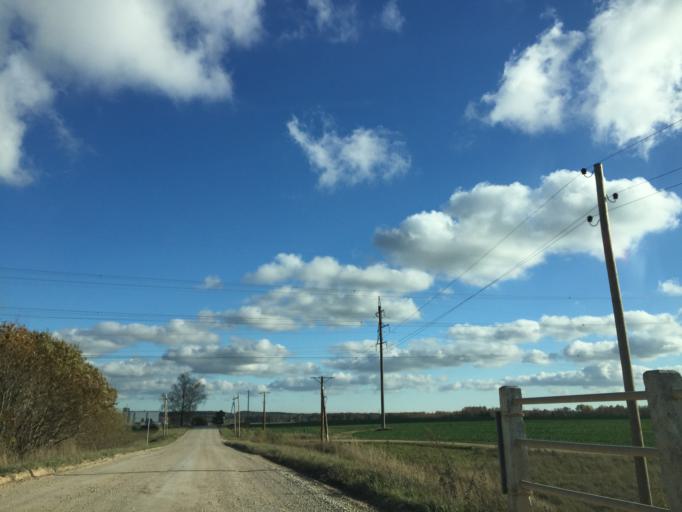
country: LV
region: Tukuma Rajons
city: Tukums
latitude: 56.9533
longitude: 23.0723
